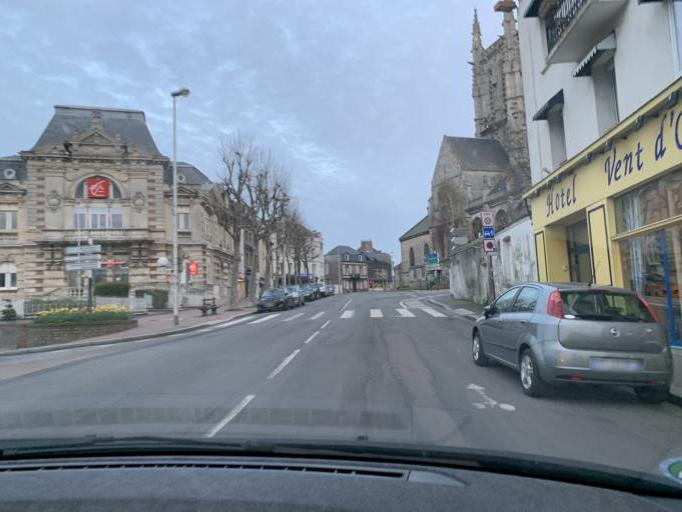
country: FR
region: Haute-Normandie
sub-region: Departement de la Seine-Maritime
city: Fecamp
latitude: 49.7587
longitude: 0.3754
